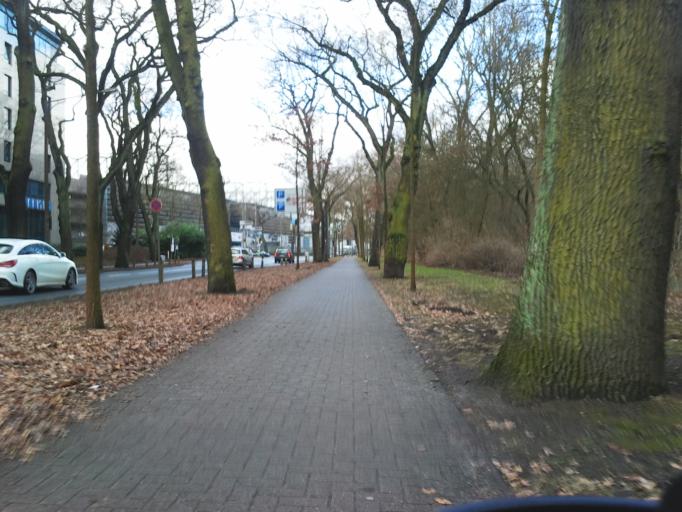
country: DE
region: Bremen
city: Bremen
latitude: 53.0879
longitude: 8.8176
